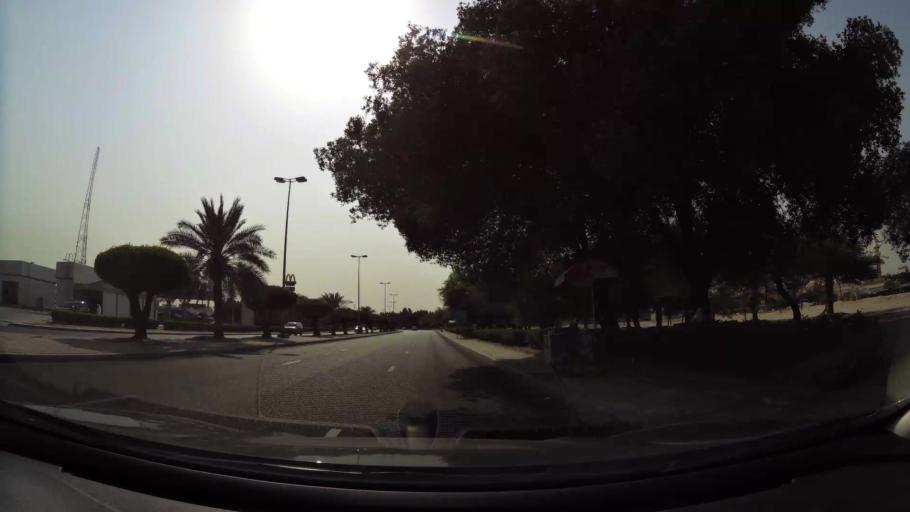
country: KW
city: Bayan
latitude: 29.3004
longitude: 48.0542
